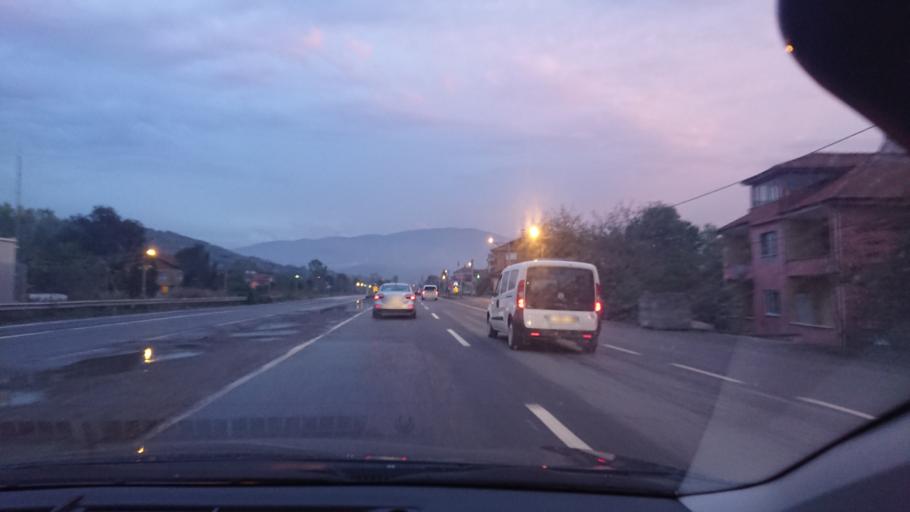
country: TR
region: Zonguldak
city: Gokcebey
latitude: 41.3307
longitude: 32.0942
